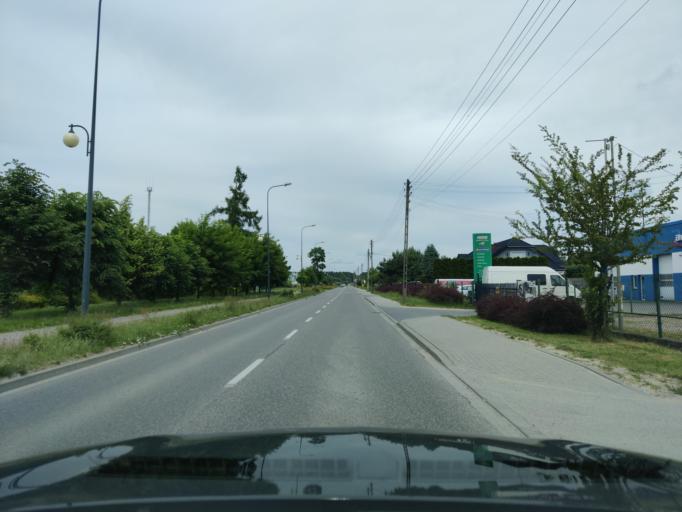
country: PL
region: Masovian Voivodeship
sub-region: Powiat wyszkowski
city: Wyszkow
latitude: 52.6124
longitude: 21.4537
